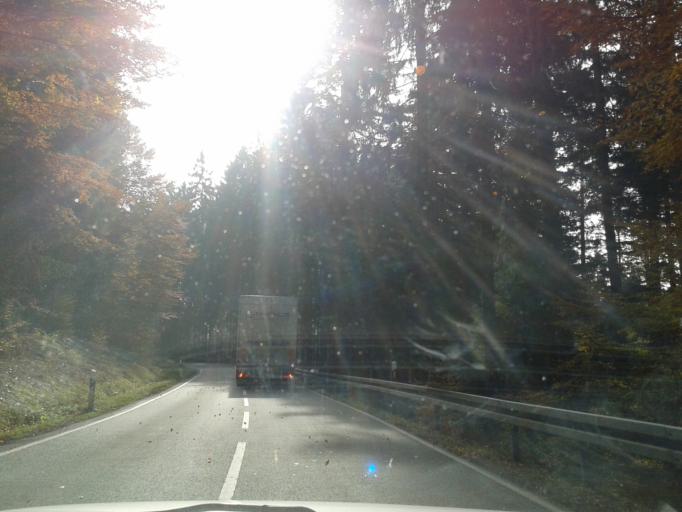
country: DE
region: North Rhine-Westphalia
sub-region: Regierungsbezirk Arnsberg
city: Bestwig
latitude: 51.3943
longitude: 8.4111
